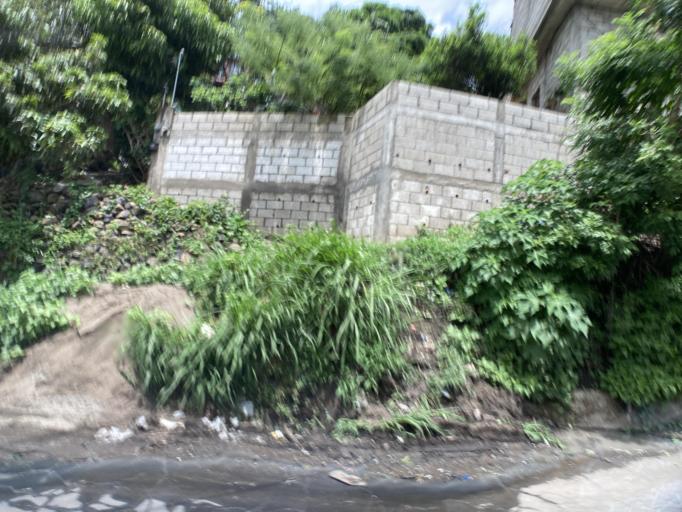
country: GT
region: Guatemala
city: Villa Canales
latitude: 14.4531
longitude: -90.5692
